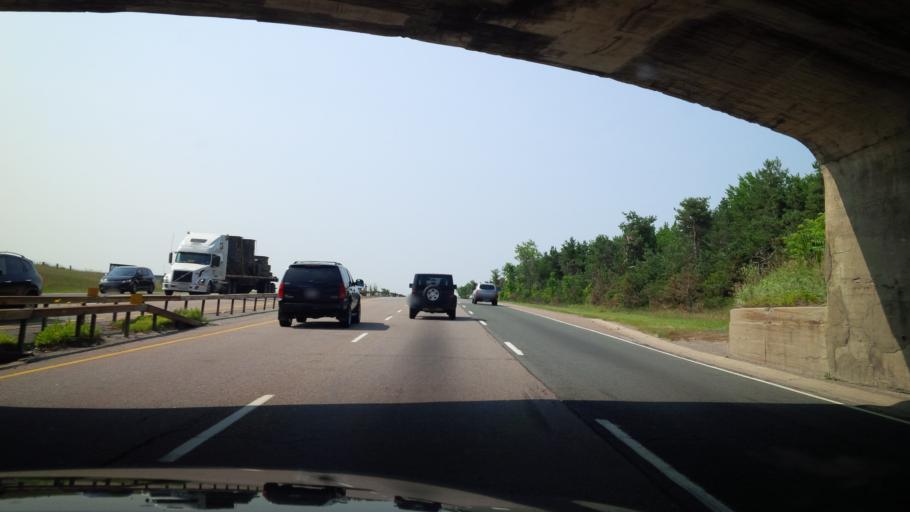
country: CA
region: Ontario
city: Innisfil
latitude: 44.3096
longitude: -79.6837
